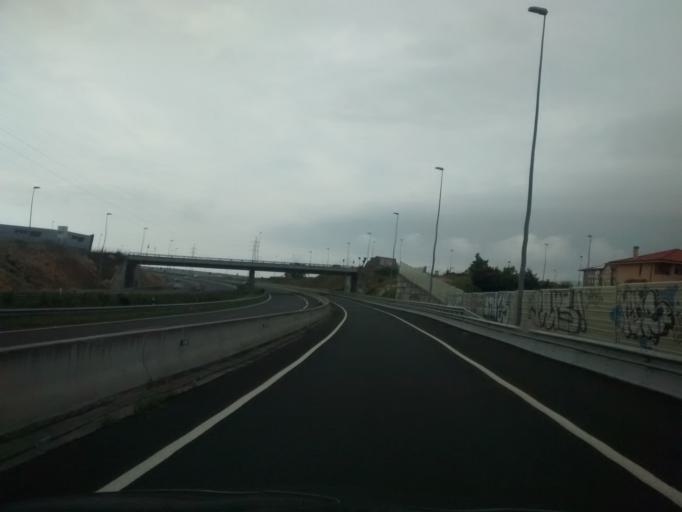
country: ES
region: Cantabria
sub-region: Provincia de Cantabria
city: Santa Cruz de Bezana
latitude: 43.4414
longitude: -3.8757
